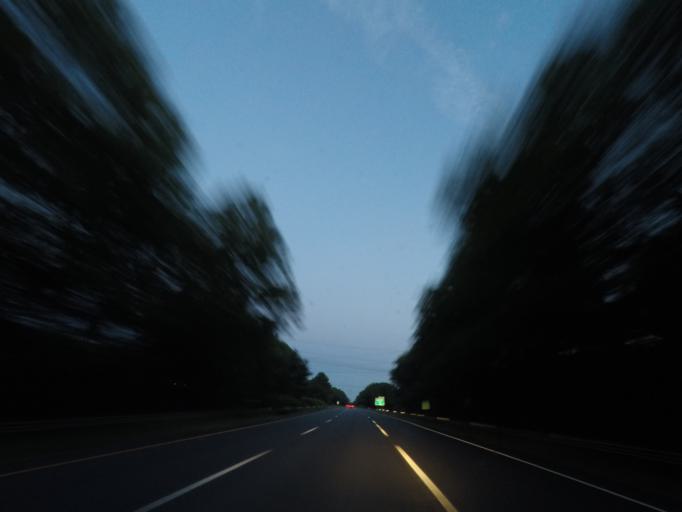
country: US
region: Connecticut
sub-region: Windham County
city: Putnam
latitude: 41.8789
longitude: -71.8958
